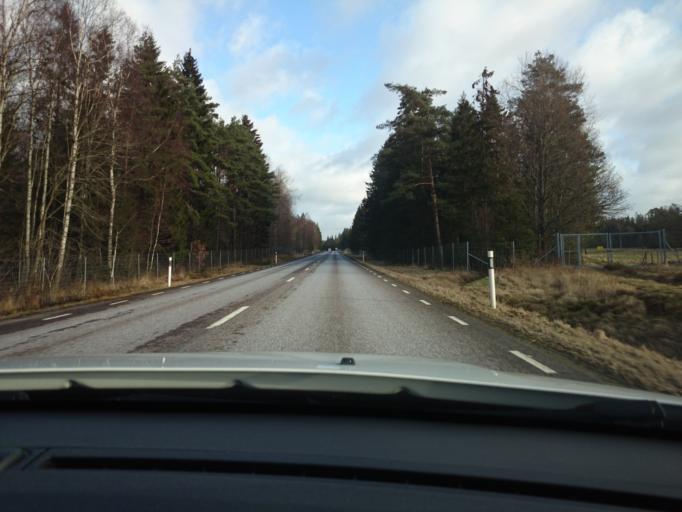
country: SE
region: Halland
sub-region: Hylte Kommun
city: Hyltebruk
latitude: 57.0235
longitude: 13.2568
